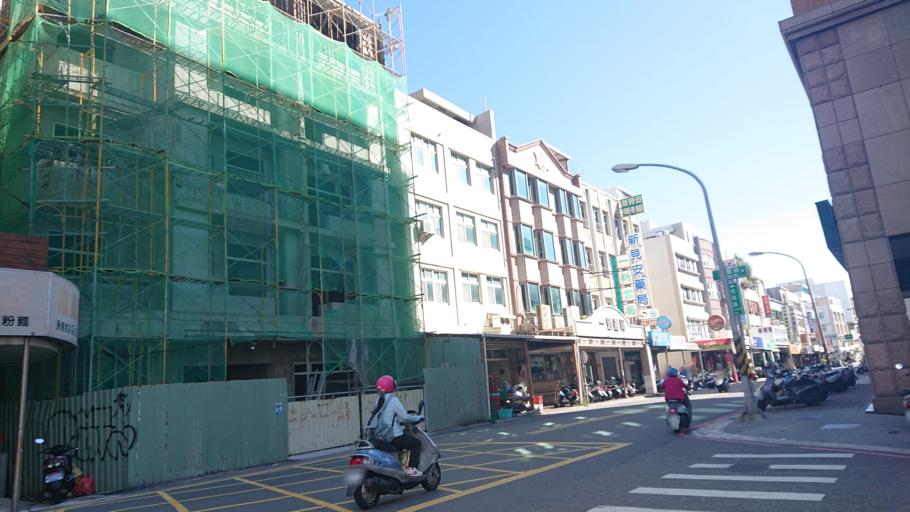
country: TW
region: Taiwan
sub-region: Penghu
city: Ma-kung
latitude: 23.5711
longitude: 119.5701
